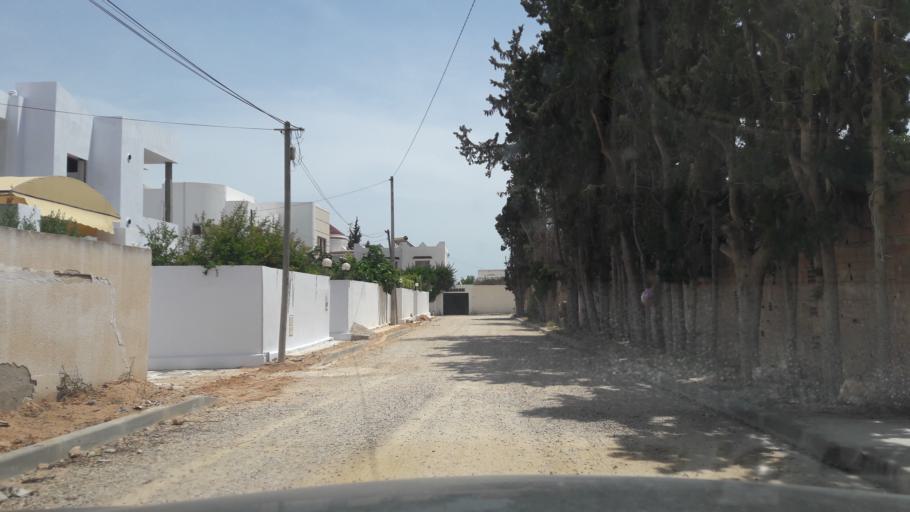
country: TN
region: Safaqis
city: Sfax
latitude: 34.7757
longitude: 10.7539
